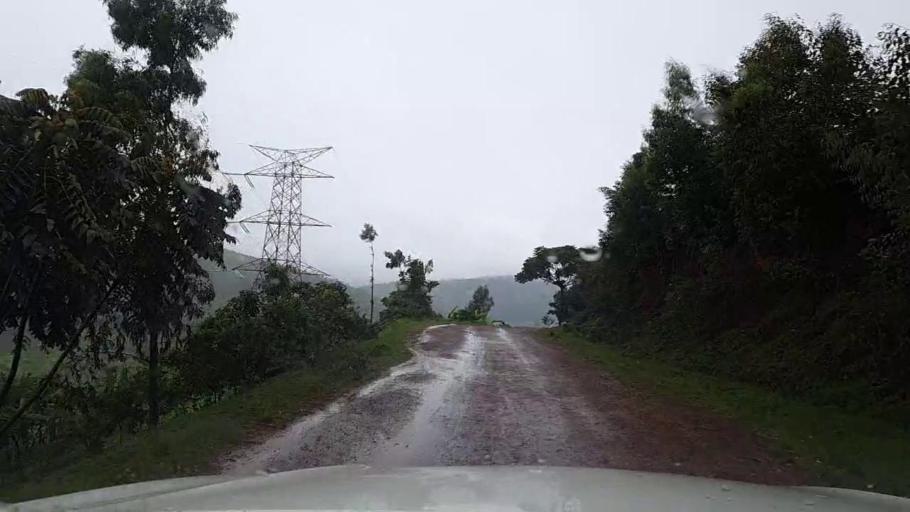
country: RW
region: Kigali
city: Kigali
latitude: -1.7647
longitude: 29.9923
